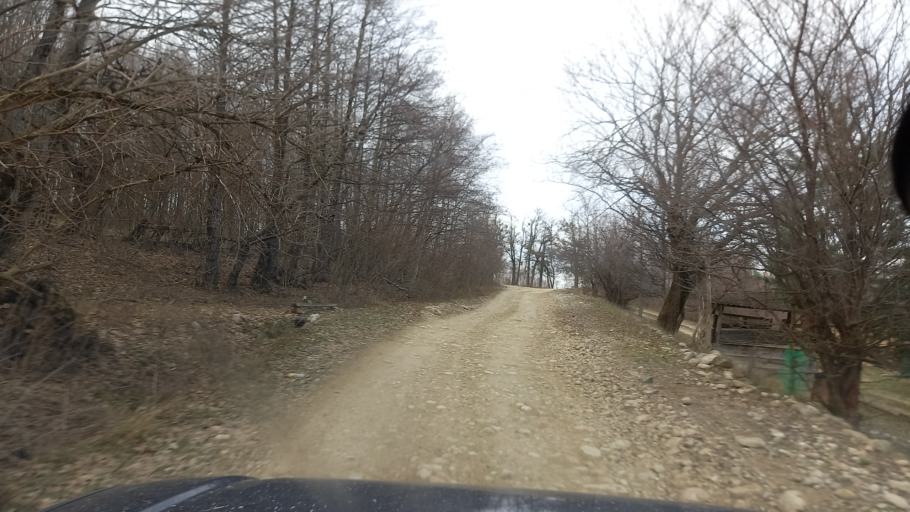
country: RU
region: Krasnodarskiy
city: Neftegorsk
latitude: 44.2278
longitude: 39.8987
